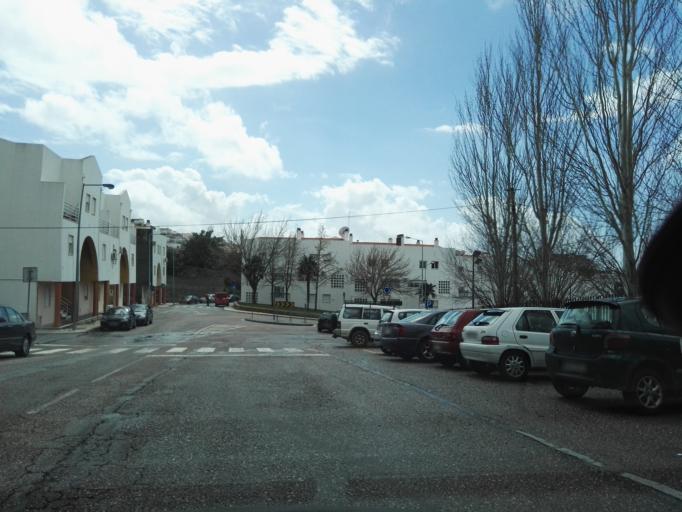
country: PT
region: Portalegre
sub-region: Portalegre
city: Portalegre
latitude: 39.2984
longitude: -7.4320
